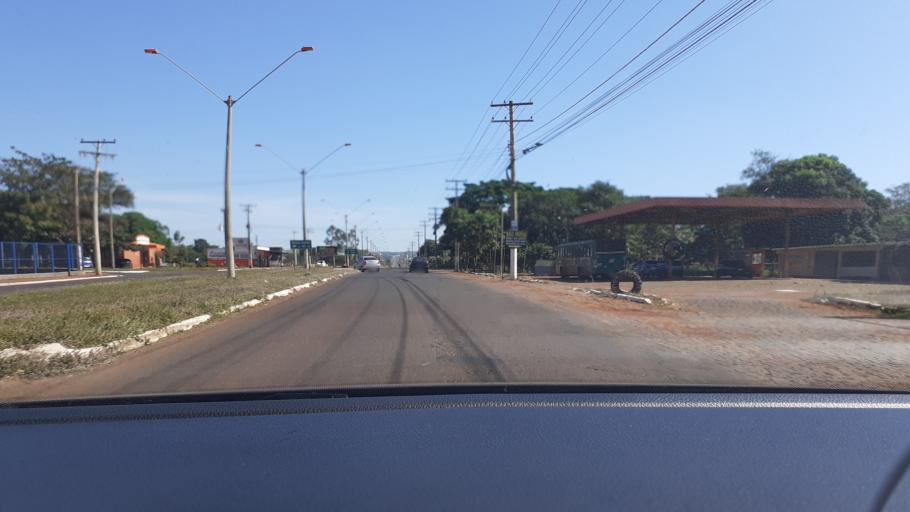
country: BR
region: Goias
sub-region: Itumbiara
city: Itumbiara
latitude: -18.4086
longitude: -49.2550
